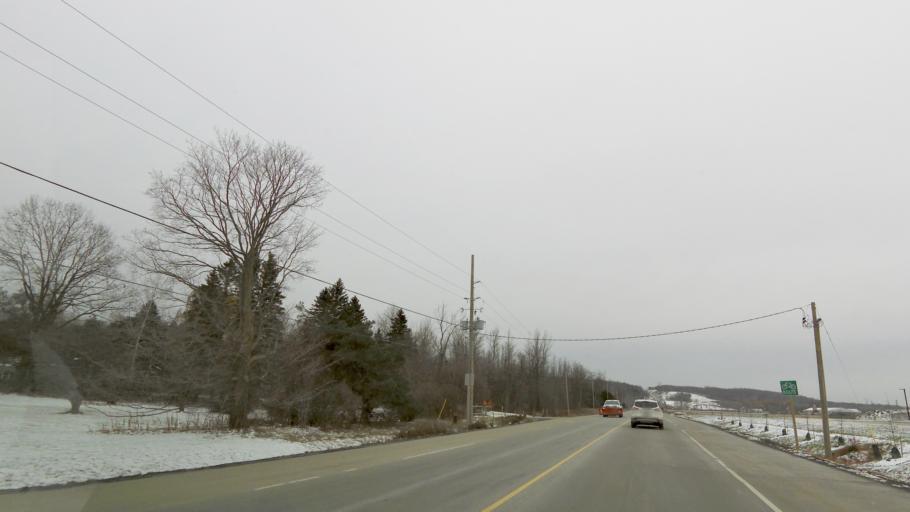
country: CA
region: Ontario
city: Newmarket
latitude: 44.1018
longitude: -79.5195
